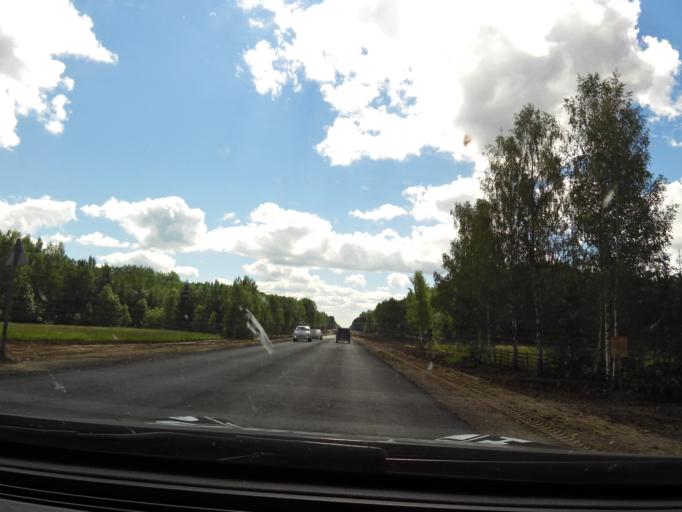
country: RU
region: Vologda
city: Molochnoye
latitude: 59.3411
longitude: 39.6797
